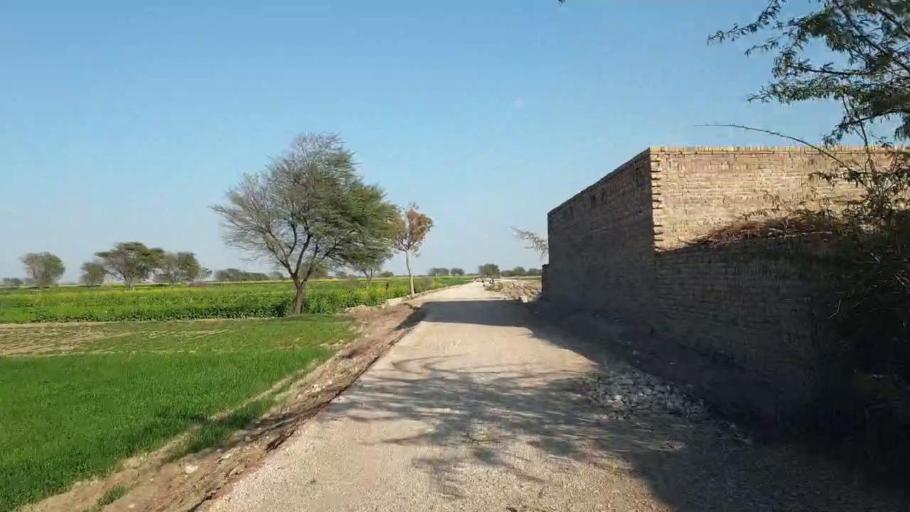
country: PK
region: Sindh
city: Shahpur Chakar
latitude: 26.1197
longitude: 68.5711
